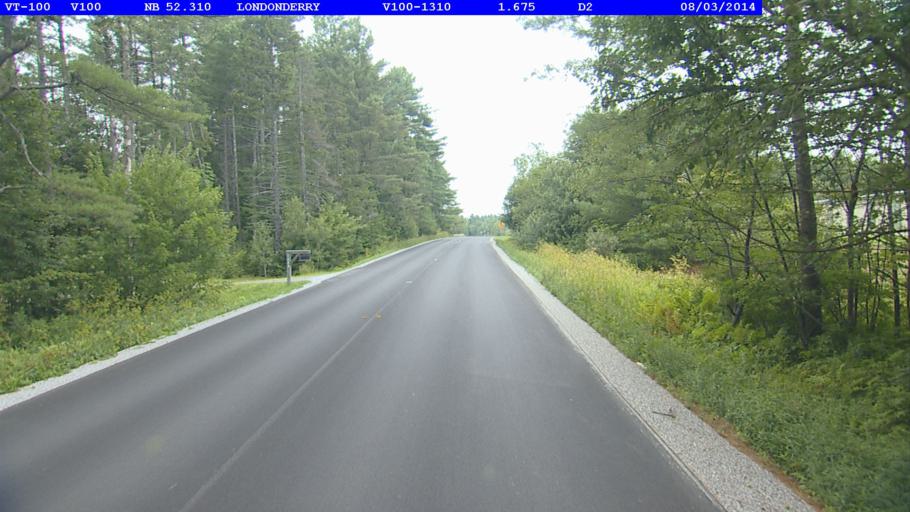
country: US
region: Vermont
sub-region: Windham County
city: Dover
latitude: 43.1755
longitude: -72.8205
